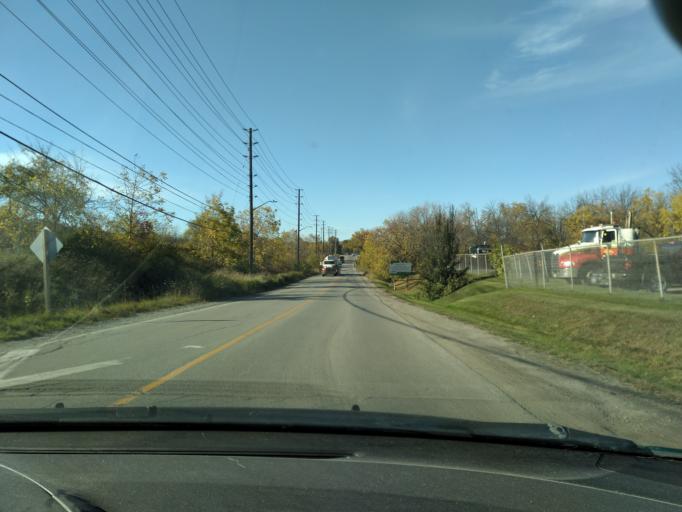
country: CA
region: Ontario
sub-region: Halton
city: Milton
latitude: 43.5146
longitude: -79.8963
